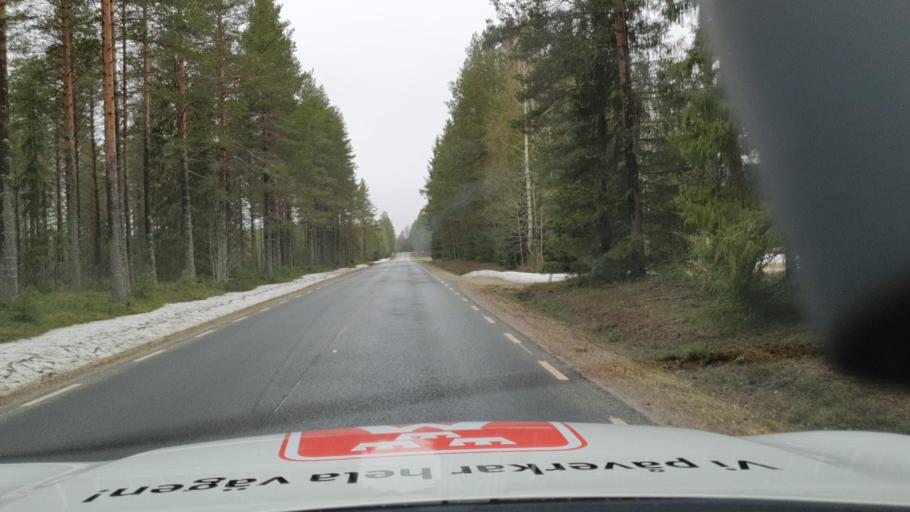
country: SE
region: Vaesterbotten
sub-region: Nordmalings Kommun
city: Nordmaling
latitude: 63.7214
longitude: 19.5468
